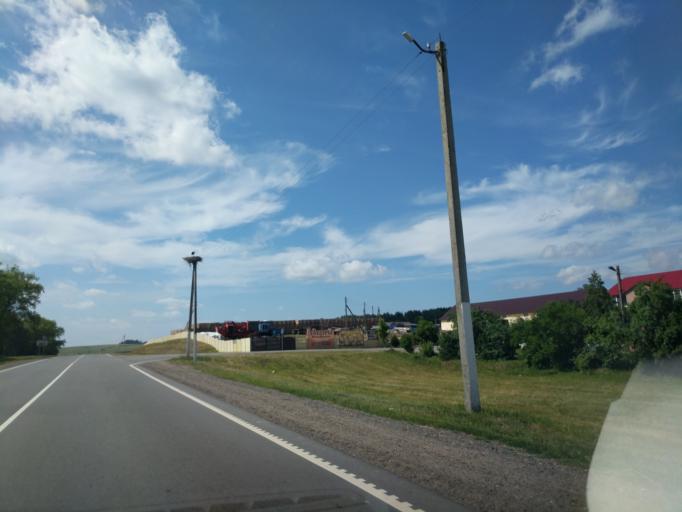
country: BY
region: Minsk
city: Syomkava
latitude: 54.1094
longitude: 27.4574
